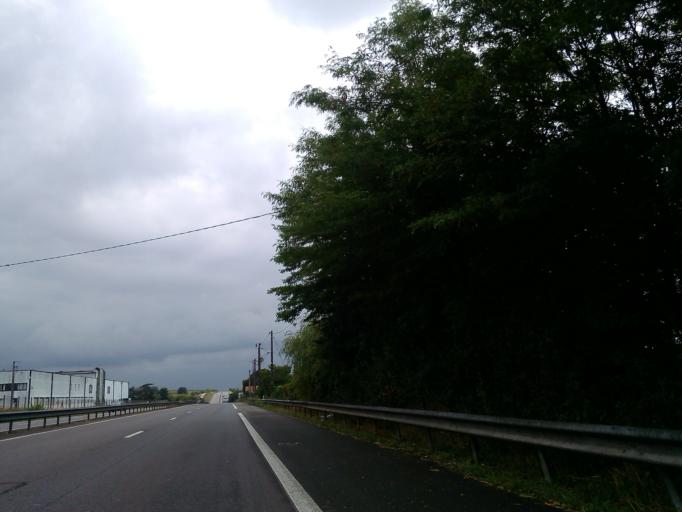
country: FR
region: Poitou-Charentes
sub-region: Departement de la Charente
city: Saint-Brice
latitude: 45.6729
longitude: -0.2637
